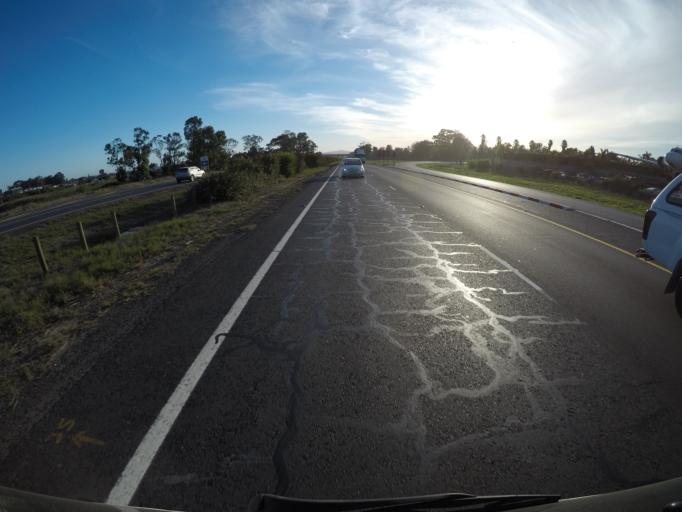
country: ZA
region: Western Cape
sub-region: City of Cape Town
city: Kraaifontein
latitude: -33.8343
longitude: 18.7394
